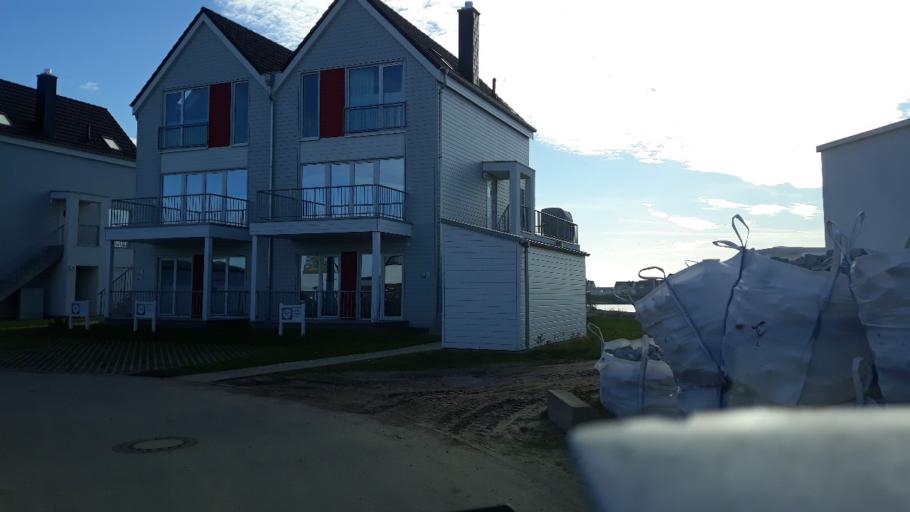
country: DE
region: Schleswig-Holstein
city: Maasholm
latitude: 54.6631
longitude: 10.0277
